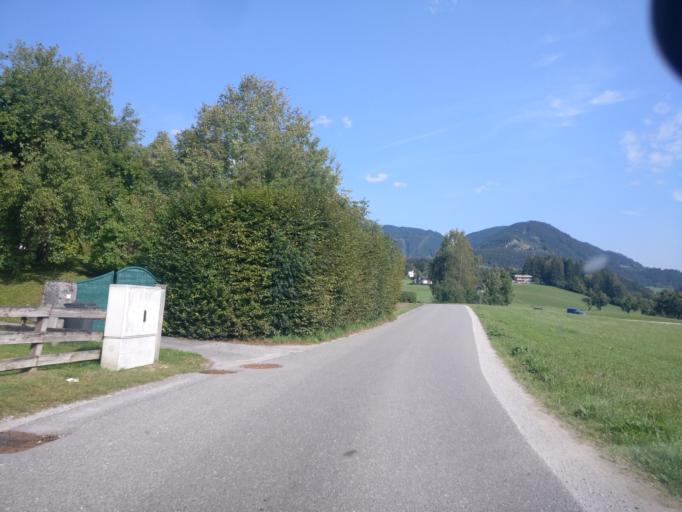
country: AT
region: Salzburg
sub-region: Politischer Bezirk Sankt Johann im Pongau
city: Pfarrwerfen
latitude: 47.4645
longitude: 13.2260
